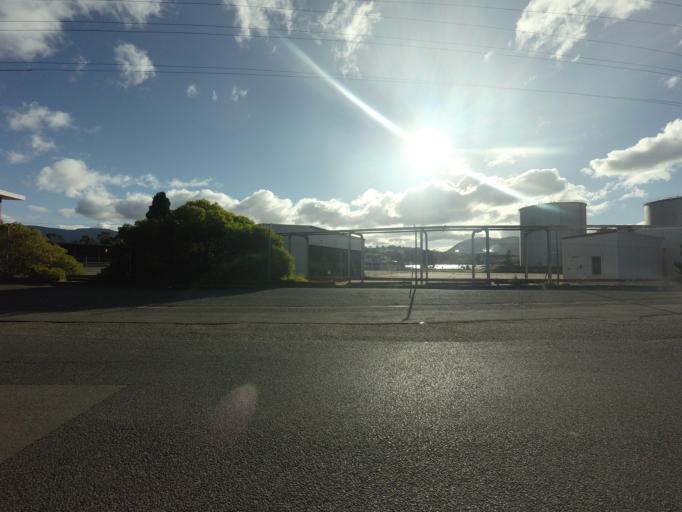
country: AU
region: Tasmania
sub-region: Glenorchy
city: Lutana
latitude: -42.8473
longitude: 147.3205
